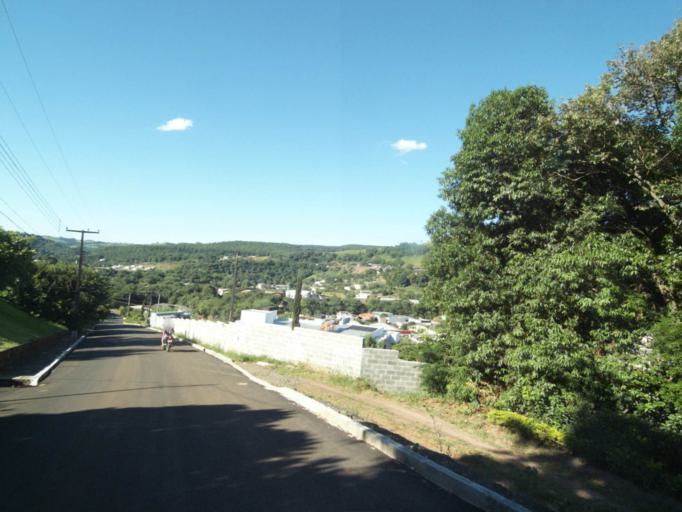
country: BR
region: Parana
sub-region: Ampere
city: Ampere
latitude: -26.1748
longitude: -53.3643
